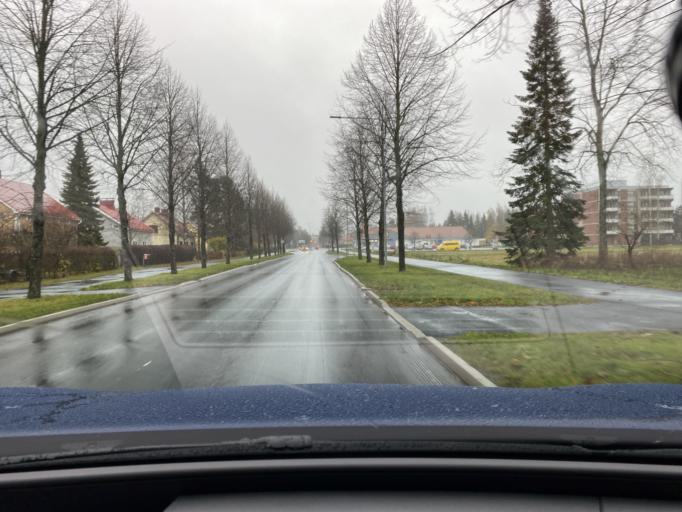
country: FI
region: Haeme
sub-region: Forssa
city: Forssa
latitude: 60.8090
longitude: 23.6191
